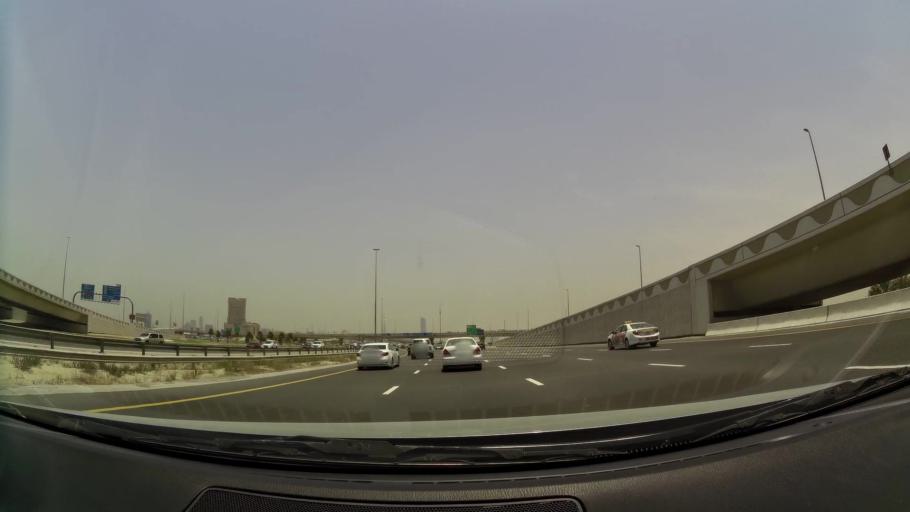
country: AE
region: Ash Shariqah
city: Sharjah
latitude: 25.2018
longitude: 55.3102
